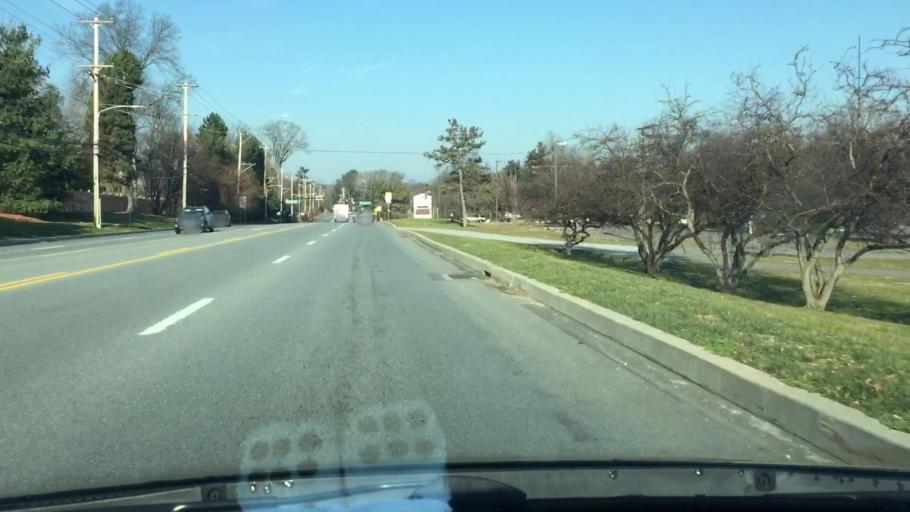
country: US
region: Pennsylvania
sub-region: Delaware County
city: Media
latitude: 39.9384
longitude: -75.3937
